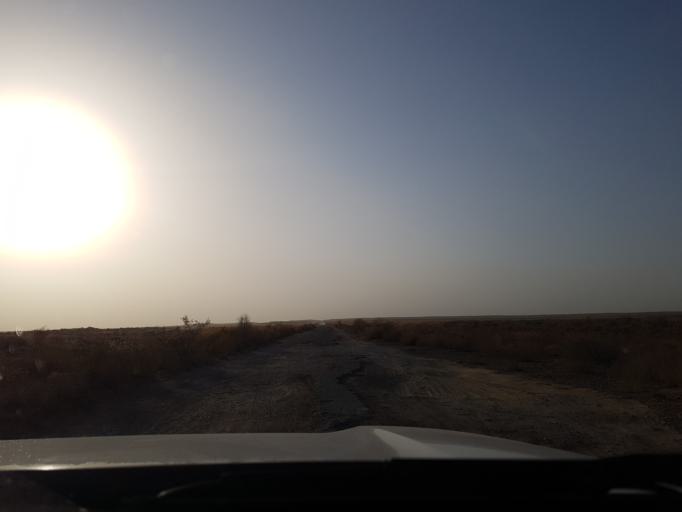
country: UZ
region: Xorazm
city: Hazorasp
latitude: 41.1652
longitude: 60.7633
